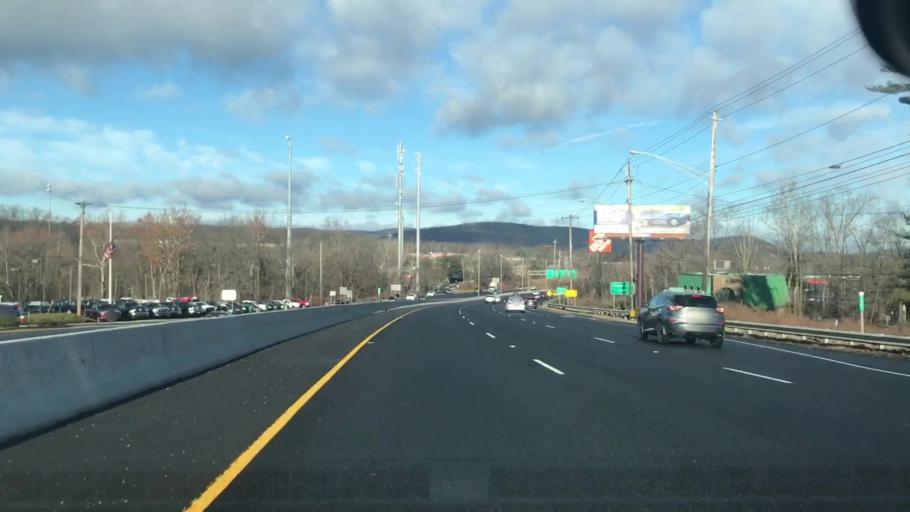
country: US
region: New Jersey
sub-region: Bergen County
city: Mahwah
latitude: 41.0768
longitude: -74.1472
